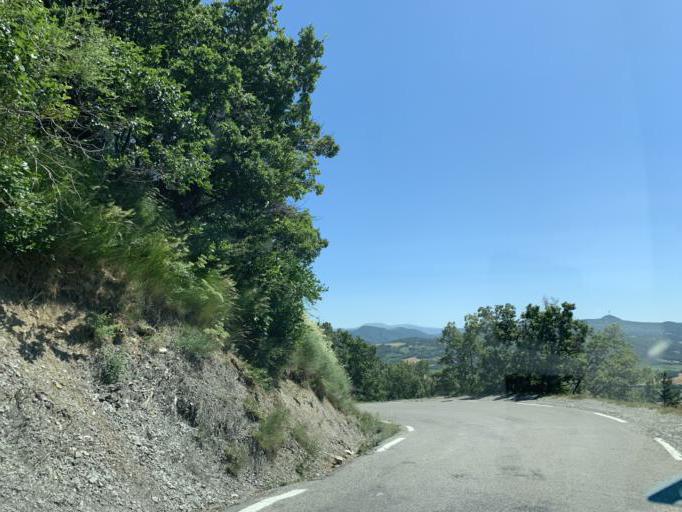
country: FR
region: Provence-Alpes-Cote d'Azur
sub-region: Departement des Hautes-Alpes
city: La Batie-Neuve
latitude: 44.5873
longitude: 6.1598
